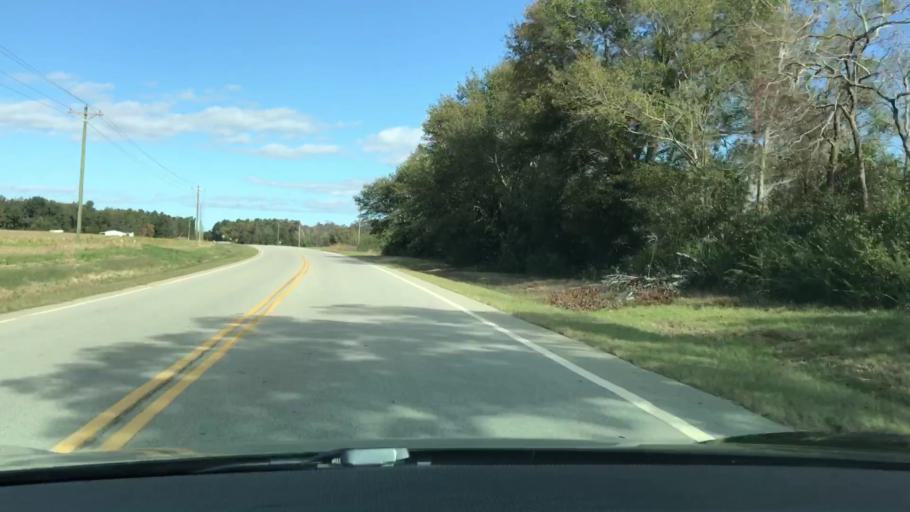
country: US
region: Georgia
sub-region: Jefferson County
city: Wrens
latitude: 33.1797
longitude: -82.4533
